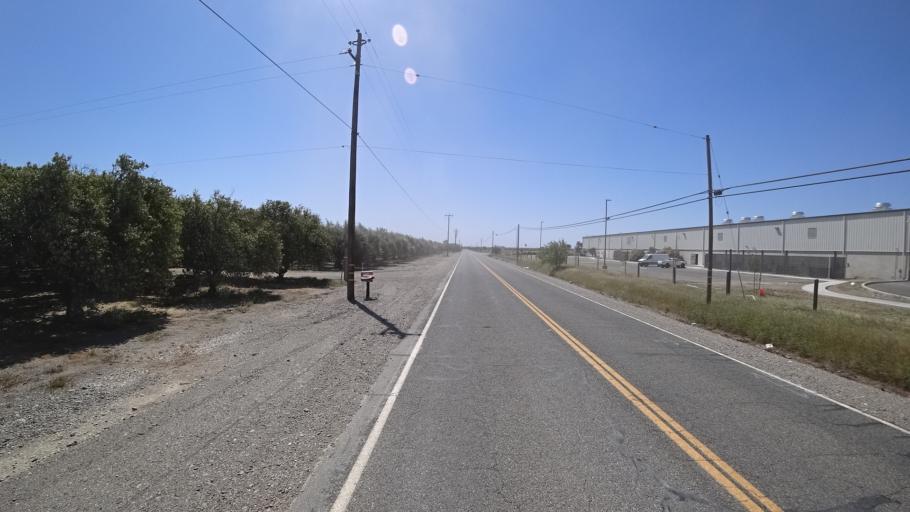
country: US
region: California
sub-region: Glenn County
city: Orland
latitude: 39.7195
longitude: -122.1410
